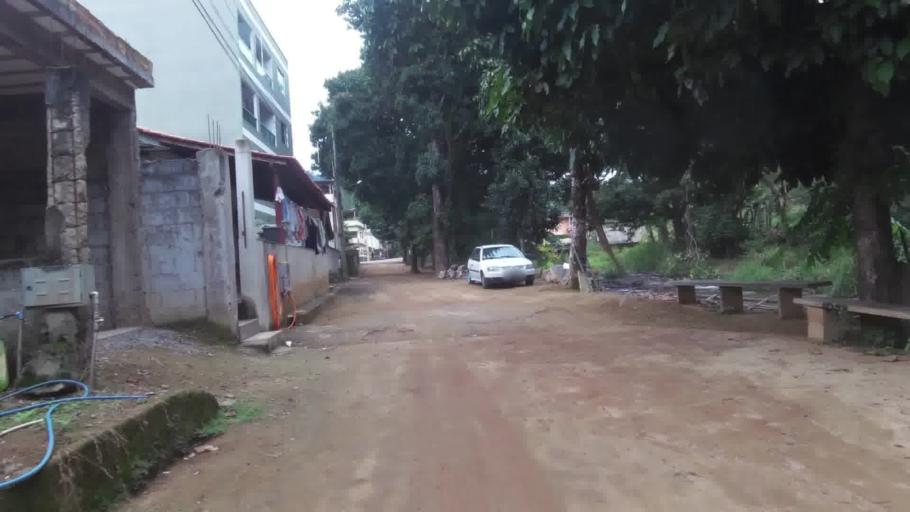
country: BR
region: Espirito Santo
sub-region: Iconha
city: Iconha
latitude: -20.7659
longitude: -40.8344
